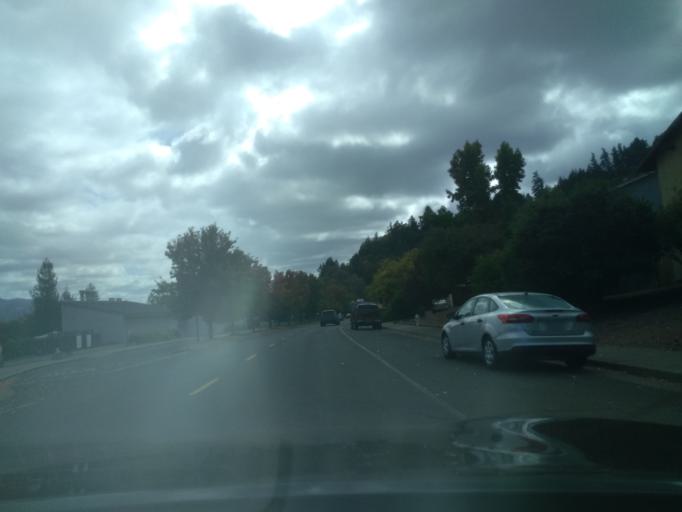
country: US
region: California
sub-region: Mendocino County
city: Ukiah
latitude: 39.1234
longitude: -123.2075
